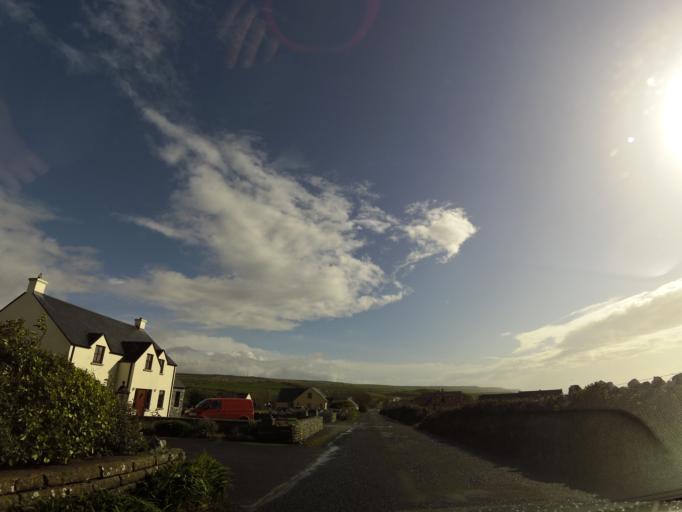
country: IE
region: Connaught
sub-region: County Galway
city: Bearna
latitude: 53.0210
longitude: -9.3699
